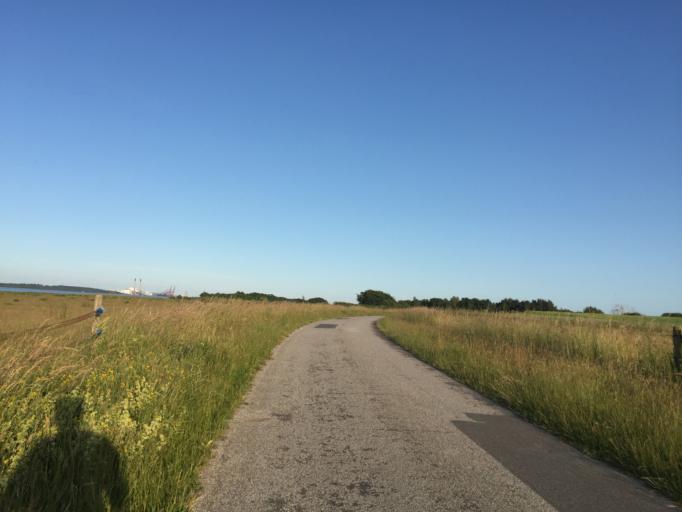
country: DK
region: Zealand
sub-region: Slagelse Kommune
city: Korsor
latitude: 55.2257
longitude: 11.1826
